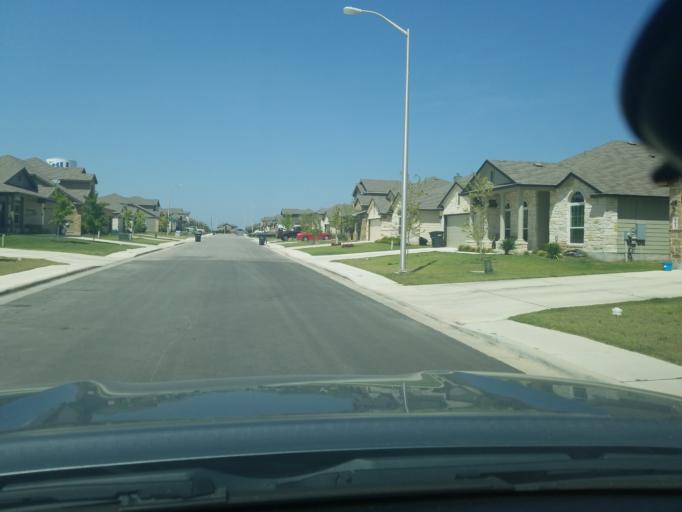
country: US
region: Texas
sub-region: Guadalupe County
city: Lake Dunlap
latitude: 29.6738
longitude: -98.0379
